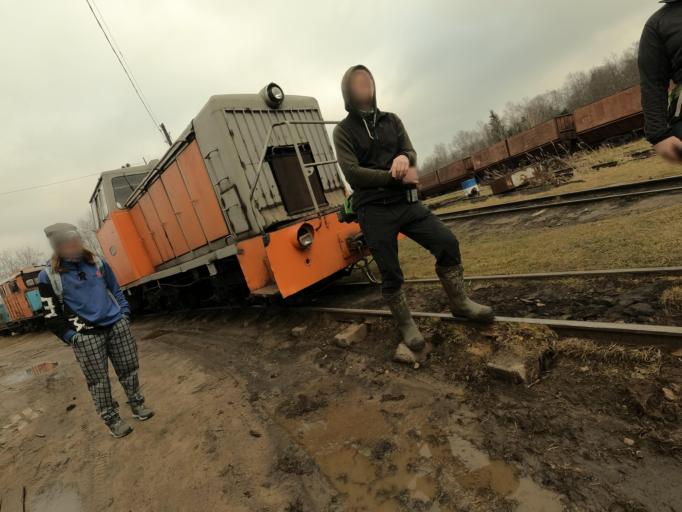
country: RU
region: Leningrad
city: Nurma
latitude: 59.6002
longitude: 31.2011
